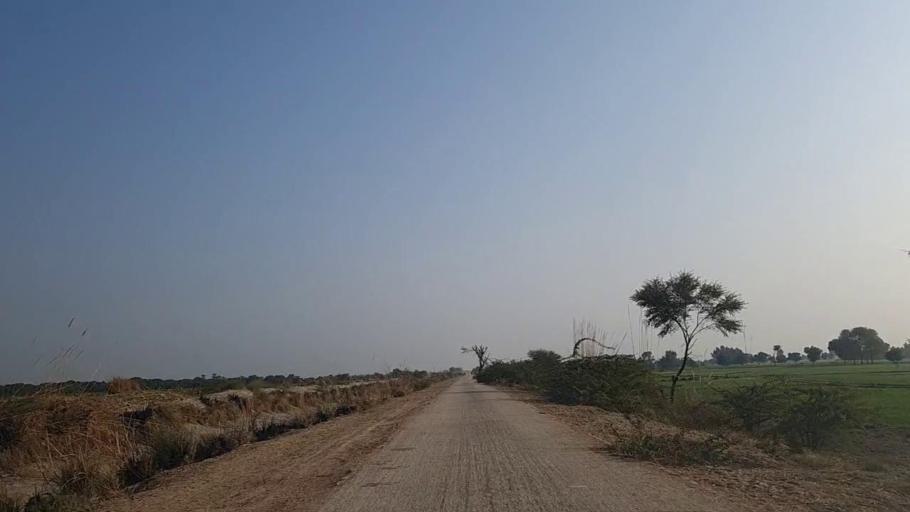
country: PK
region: Sindh
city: Jam Sahib
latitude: 26.2350
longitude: 68.5929
